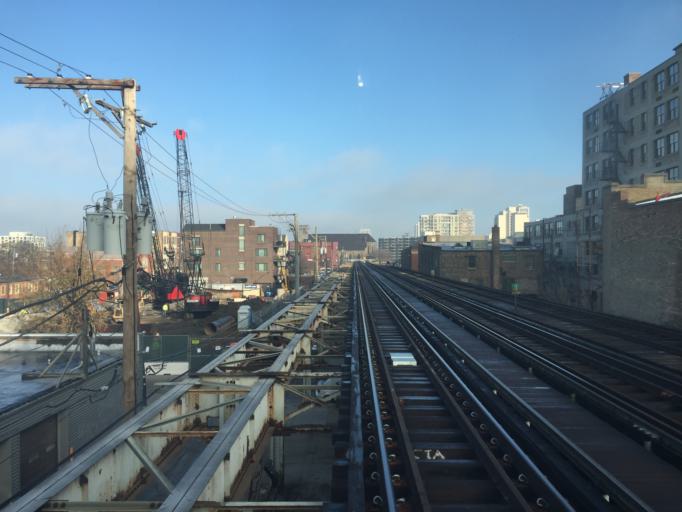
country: US
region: Illinois
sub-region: Cook County
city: Chicago
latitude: 41.8987
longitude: -87.6366
